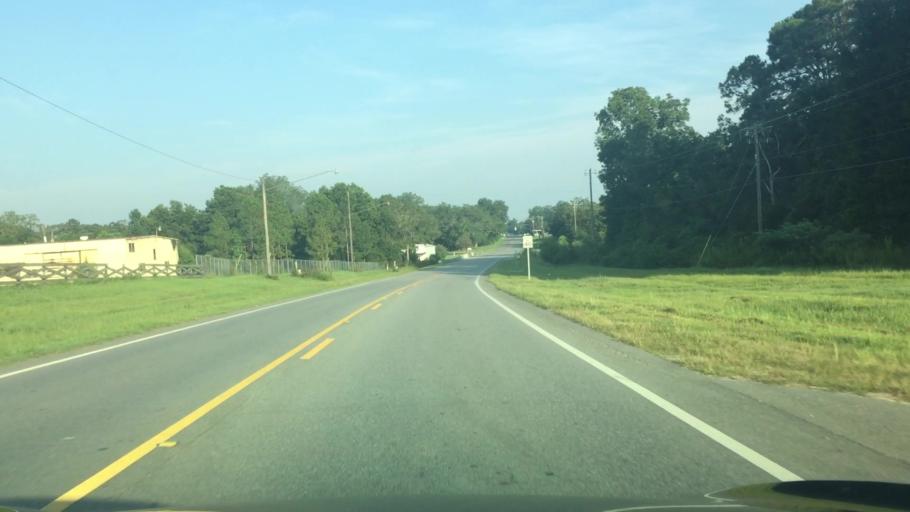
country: US
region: Alabama
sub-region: Covington County
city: Florala
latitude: 31.0089
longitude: -86.3435
